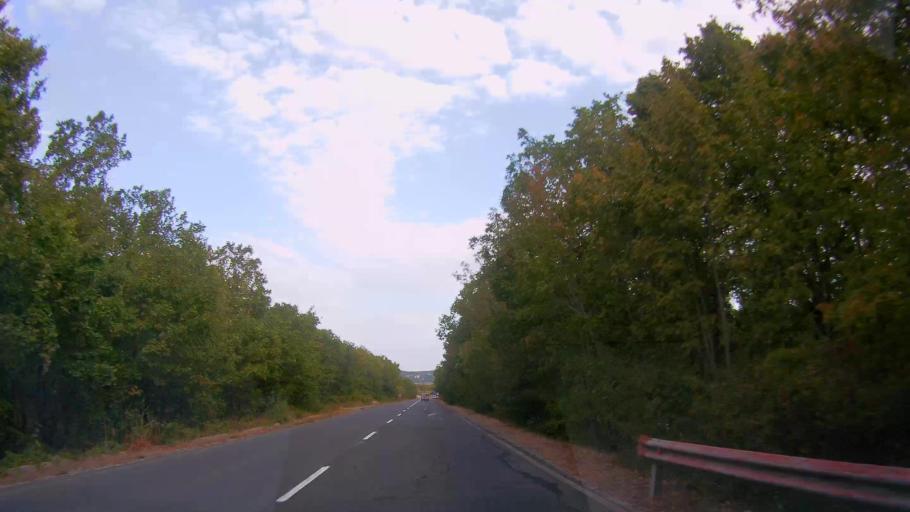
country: BG
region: Burgas
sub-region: Obshtina Sozopol
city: Sozopol
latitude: 42.3419
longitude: 27.7164
